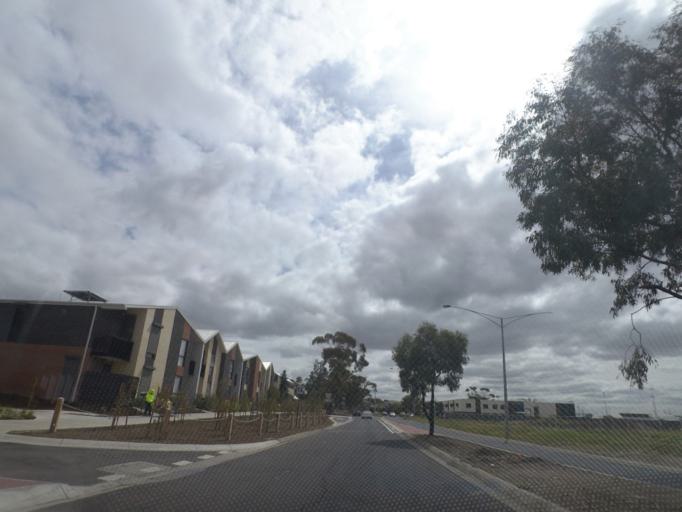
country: AU
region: Victoria
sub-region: Brimbank
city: Cairnlea
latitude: -37.7572
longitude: 144.7914
